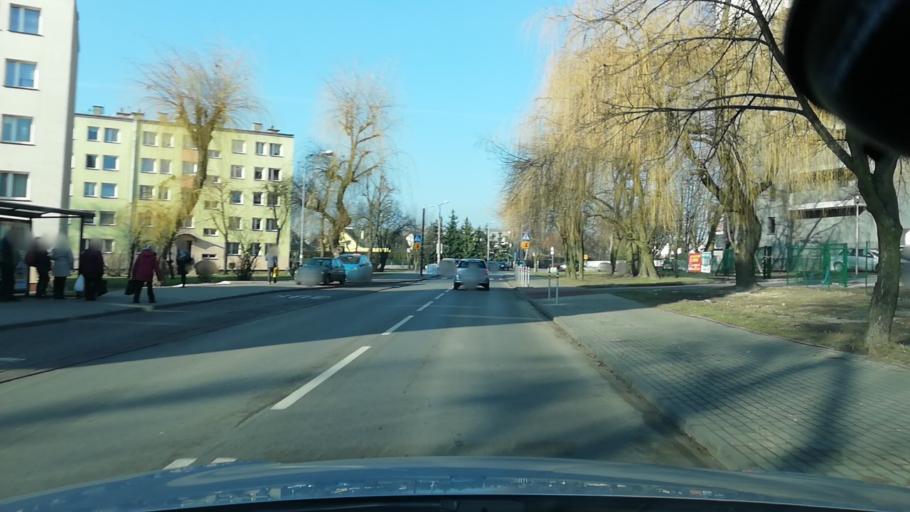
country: PL
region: Silesian Voivodeship
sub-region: Swietochlowice
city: Swietochlowice
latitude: 50.2679
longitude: 18.9326
